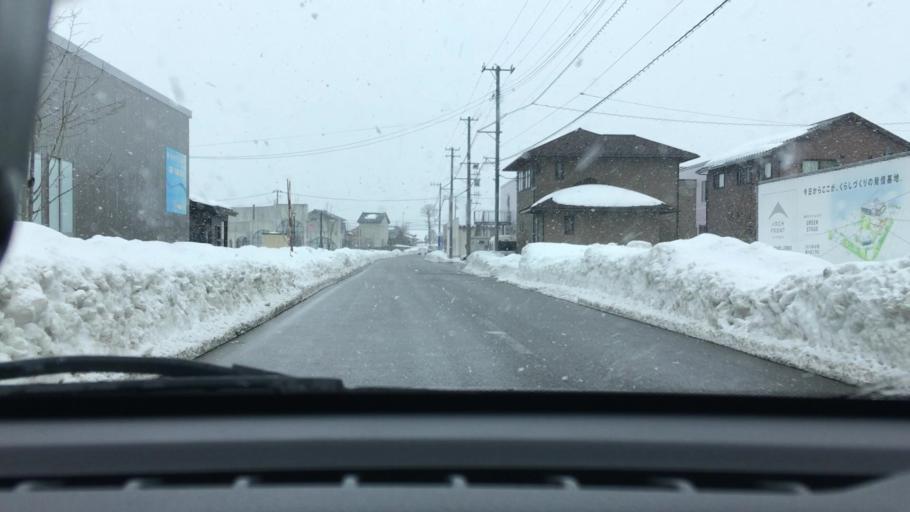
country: JP
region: Niigata
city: Joetsu
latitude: 37.1618
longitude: 138.2503
